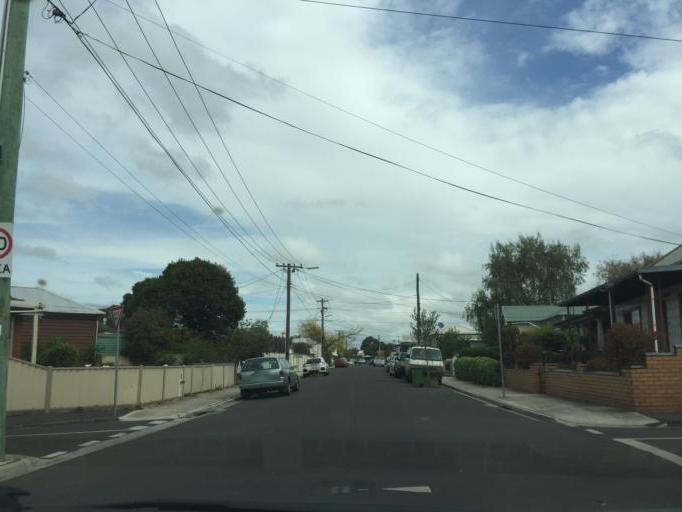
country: AU
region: Victoria
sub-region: Maribyrnong
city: Seddon
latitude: -37.8031
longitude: 144.8885
